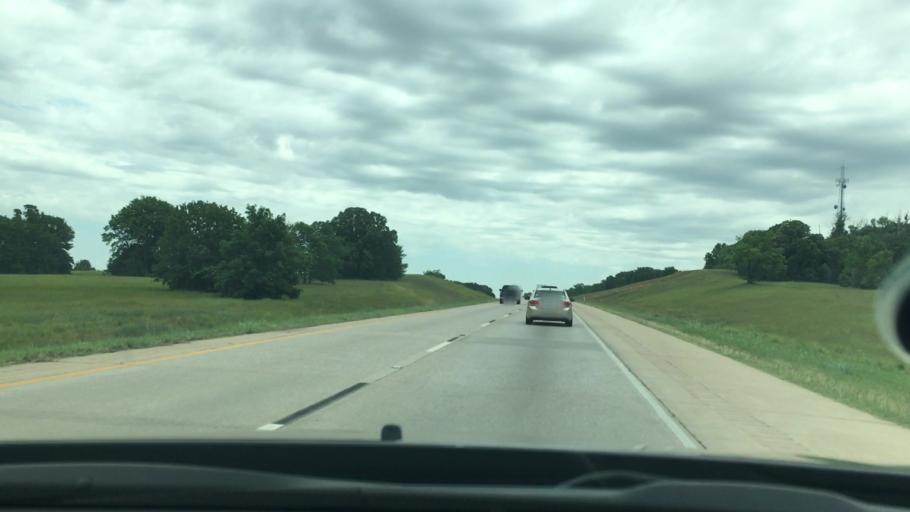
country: US
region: Oklahoma
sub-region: Love County
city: Marietta
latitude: 34.0048
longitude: -97.1427
